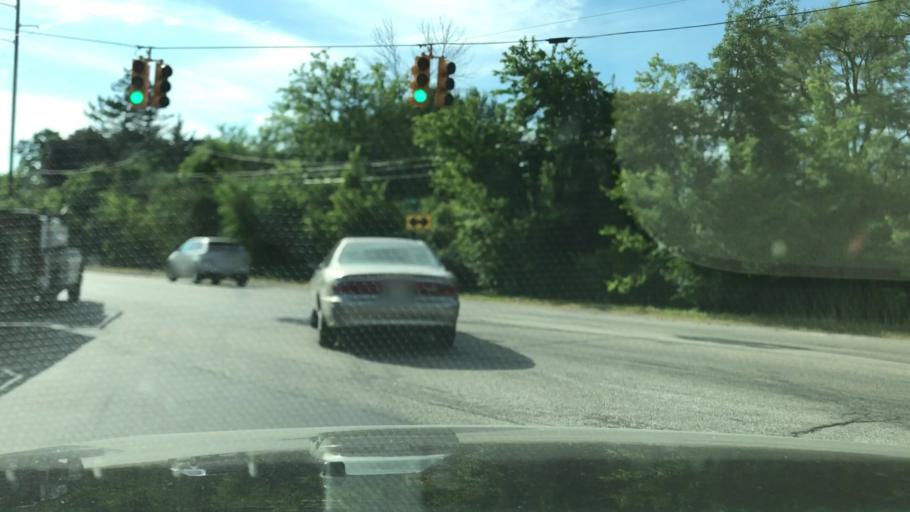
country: US
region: Michigan
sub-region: Kent County
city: East Grand Rapids
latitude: 42.9627
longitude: -85.6079
